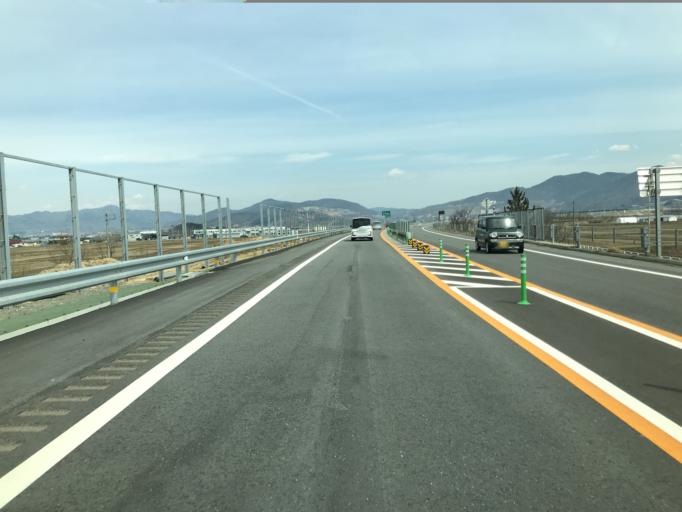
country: JP
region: Yamagata
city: Takahata
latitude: 38.0185
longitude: 140.1587
